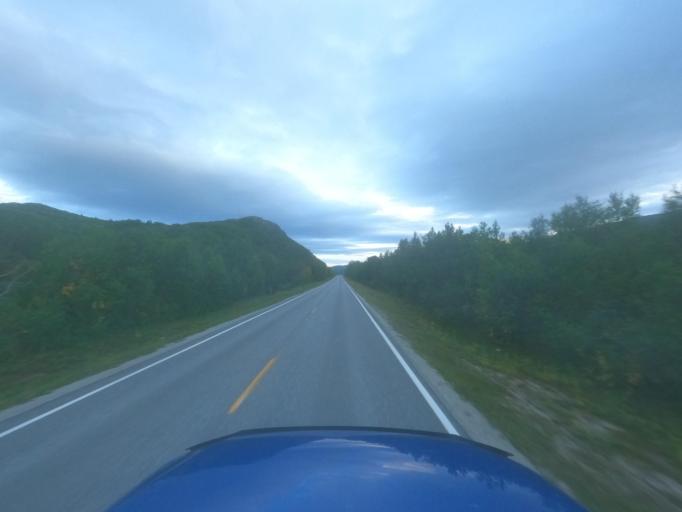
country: NO
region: Finnmark Fylke
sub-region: Porsanger
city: Lakselv
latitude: 69.9237
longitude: 24.9819
